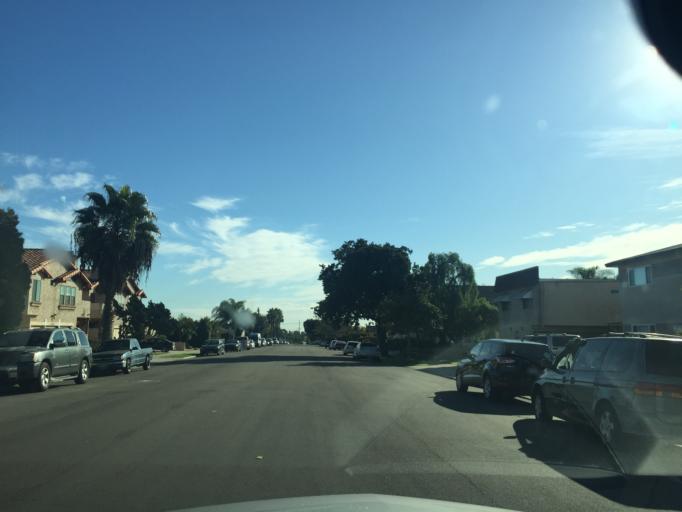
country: US
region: California
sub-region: San Diego County
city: San Diego
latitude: 32.7532
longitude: -117.1205
